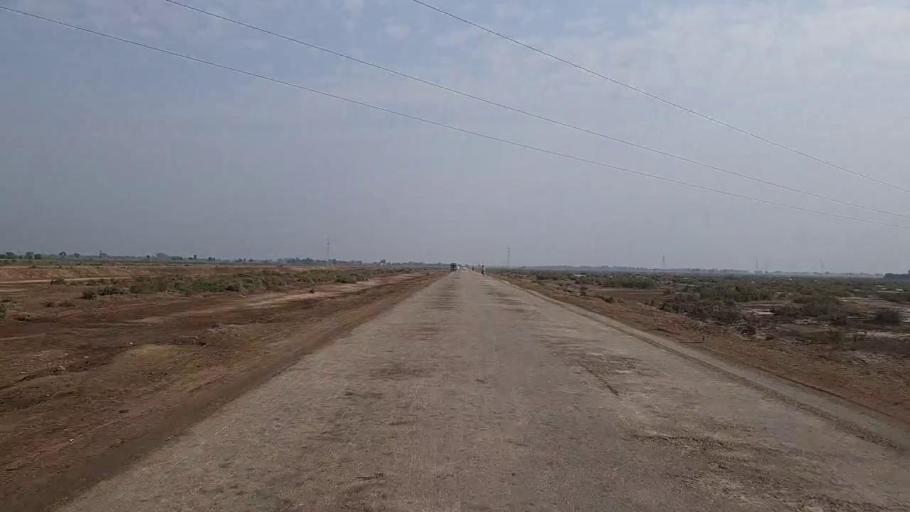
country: PK
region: Sindh
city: Mirpur Khas
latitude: 25.4236
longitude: 69.0221
